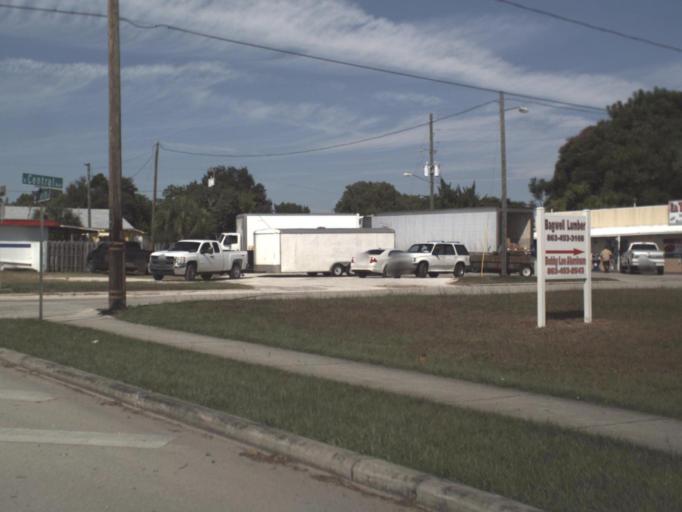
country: US
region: Florida
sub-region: Highlands County
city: Avon Park
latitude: 27.5959
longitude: -81.5060
